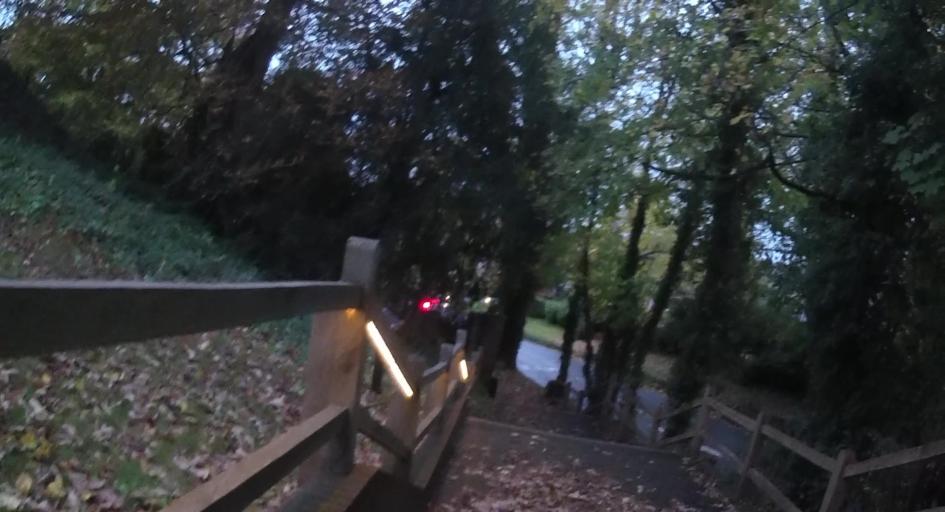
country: GB
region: England
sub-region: Surrey
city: Farnham
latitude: 51.2180
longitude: -0.8026
